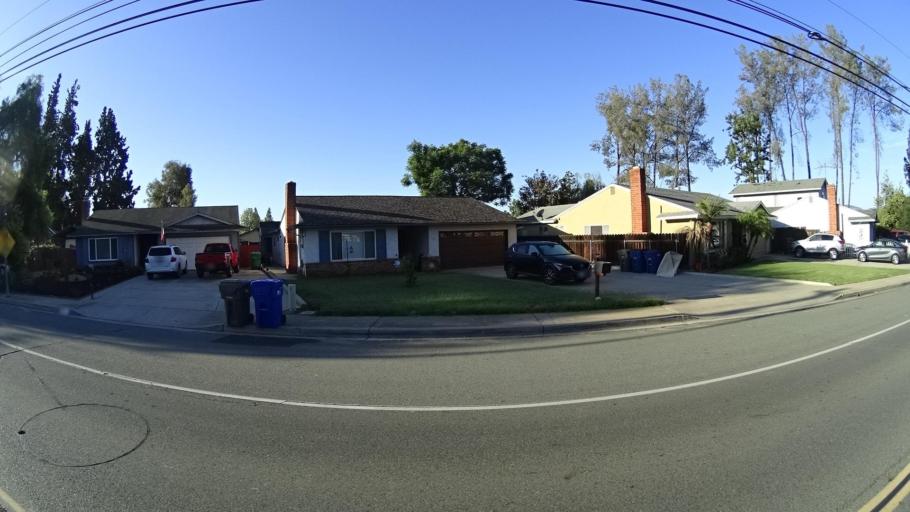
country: US
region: California
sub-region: San Diego County
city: Winter Gardens
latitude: 32.8216
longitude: -116.9455
